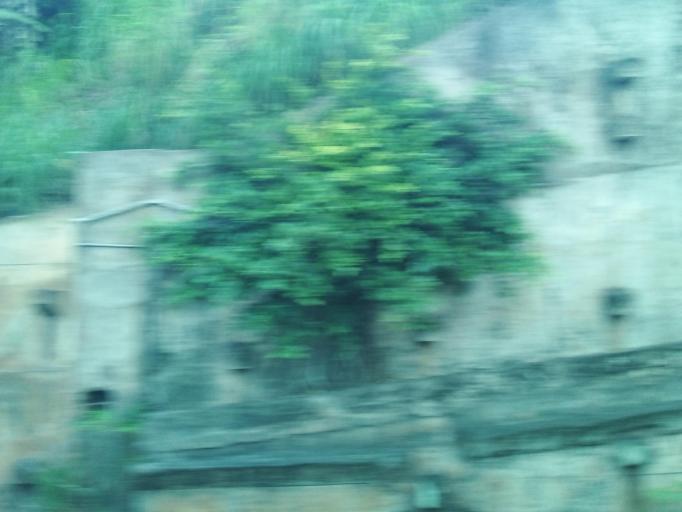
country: BR
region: Minas Gerais
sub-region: Joao Monlevade
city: Joao Monlevade
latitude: -19.8287
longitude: -43.1274
